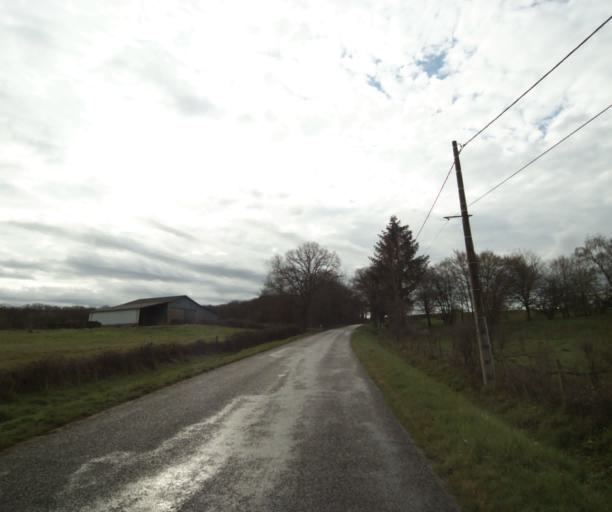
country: FR
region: Auvergne
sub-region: Departement de l'Allier
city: Toulon-sur-Allier
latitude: 46.5236
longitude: 3.4167
